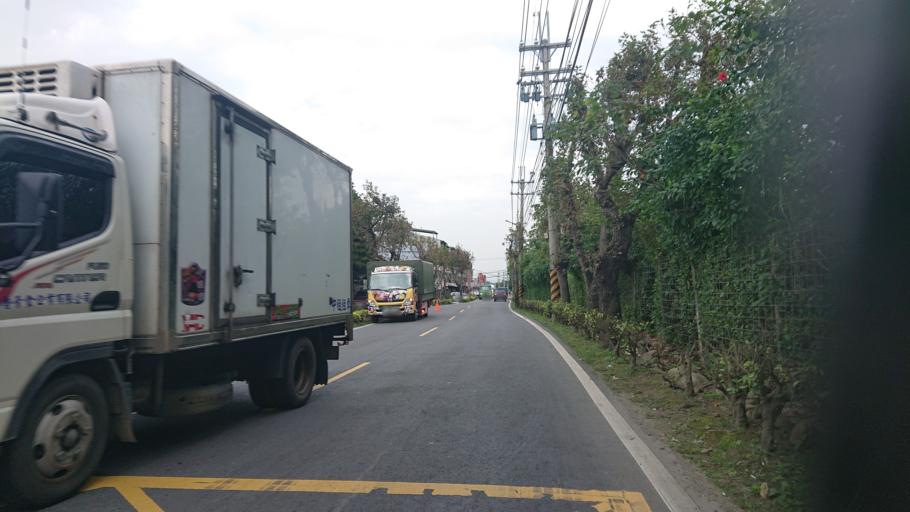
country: TW
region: Taiwan
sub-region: Taoyuan
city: Taoyuan
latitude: 24.9512
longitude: 121.3721
